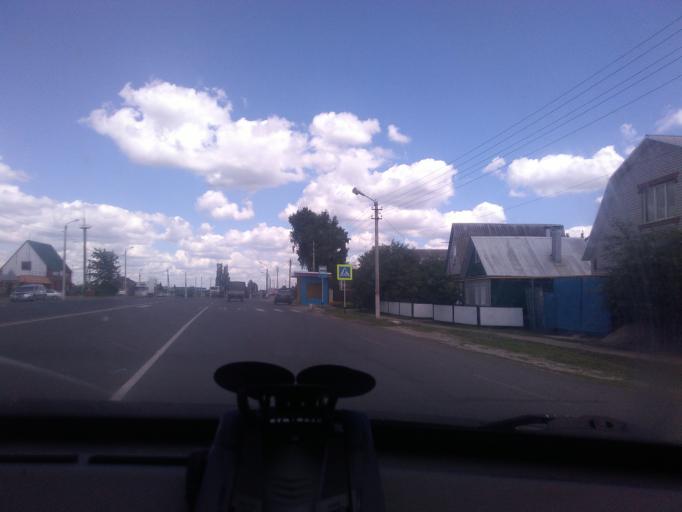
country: RU
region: Kursk
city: Voroshnevo
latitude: 51.6520
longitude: 35.9926
